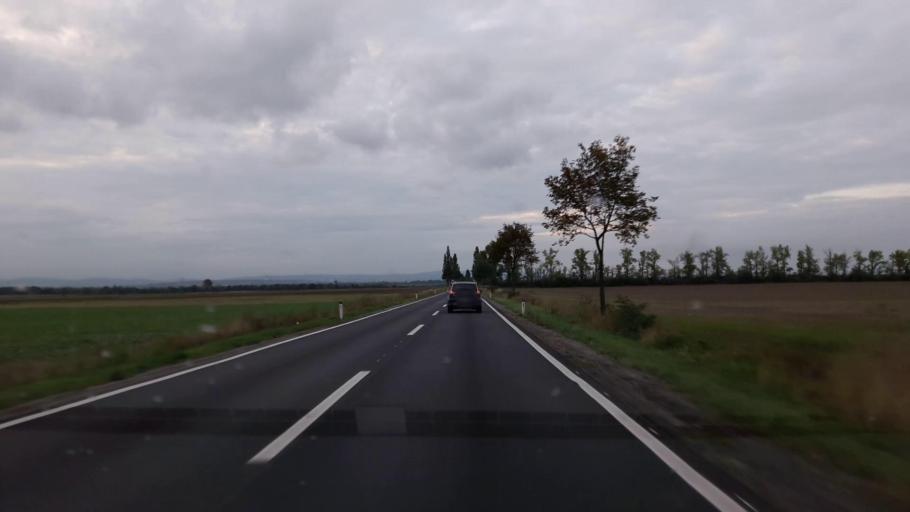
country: AT
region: Lower Austria
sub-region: Politischer Bezirk Wien-Umgebung
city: Rauchenwarth
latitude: 48.1021
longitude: 16.5356
